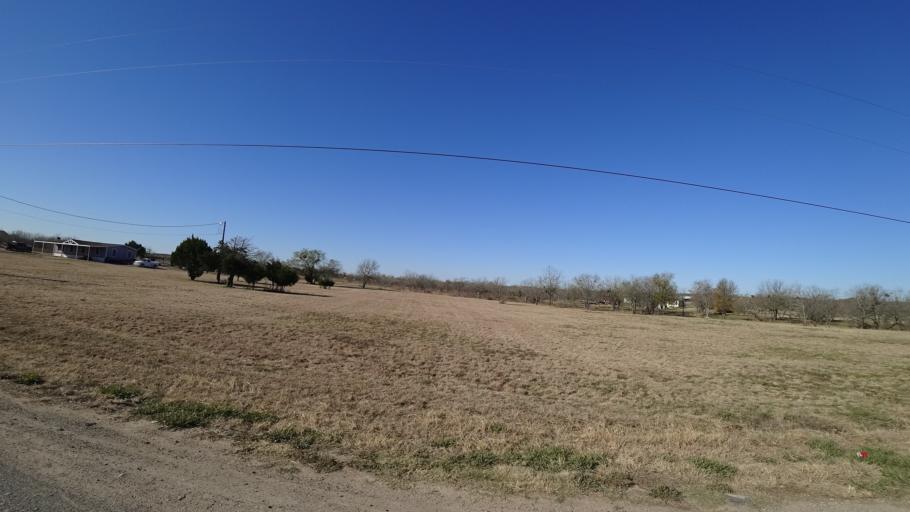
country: US
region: Texas
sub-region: Travis County
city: Onion Creek
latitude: 30.1068
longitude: -97.6771
